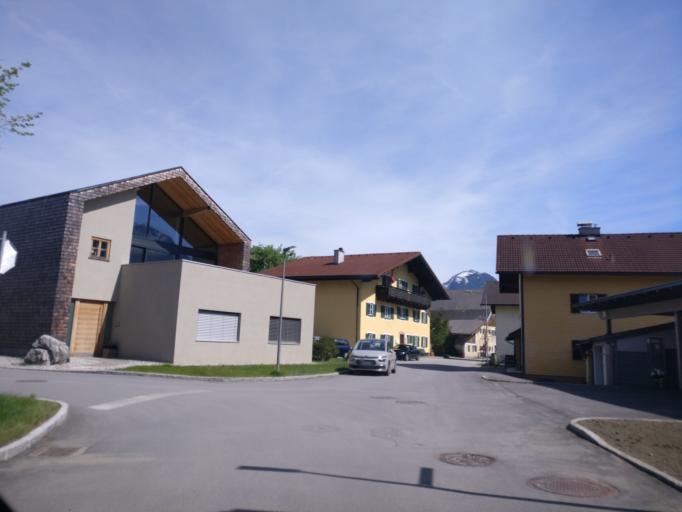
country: AT
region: Salzburg
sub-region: Politischer Bezirk Hallein
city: Kuchl
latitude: 47.6379
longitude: 13.1469
